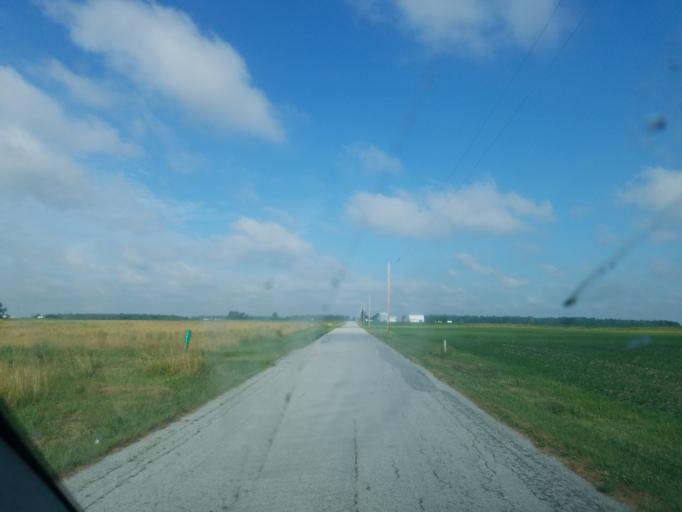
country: US
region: Ohio
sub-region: Hardin County
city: Kenton
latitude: 40.7179
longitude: -83.6797
